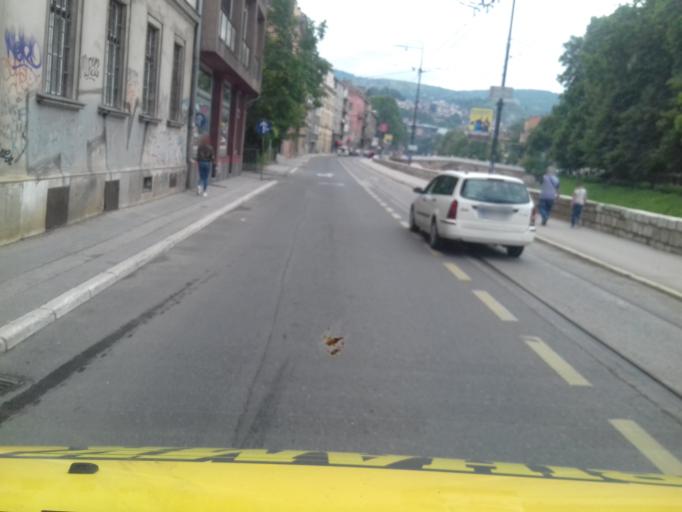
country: BA
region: Federation of Bosnia and Herzegovina
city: Kobilja Glava
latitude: 43.8573
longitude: 18.4269
